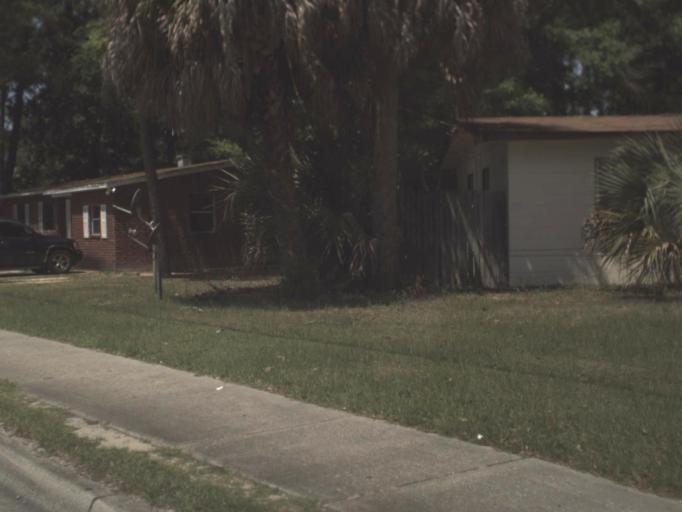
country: US
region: Florida
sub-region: Escambia County
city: Goulding
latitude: 30.4543
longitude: -87.2165
